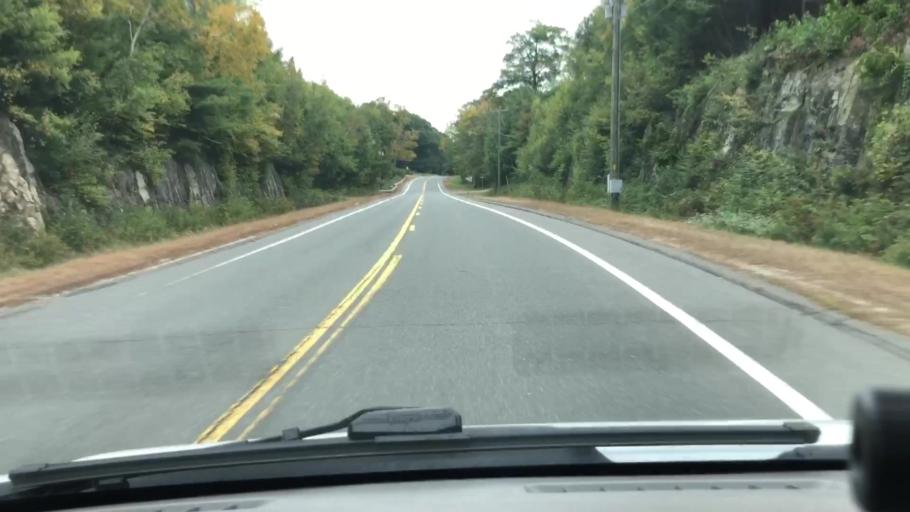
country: US
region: Massachusetts
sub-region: Hampshire County
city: Westhampton
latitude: 42.2828
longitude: -72.8149
